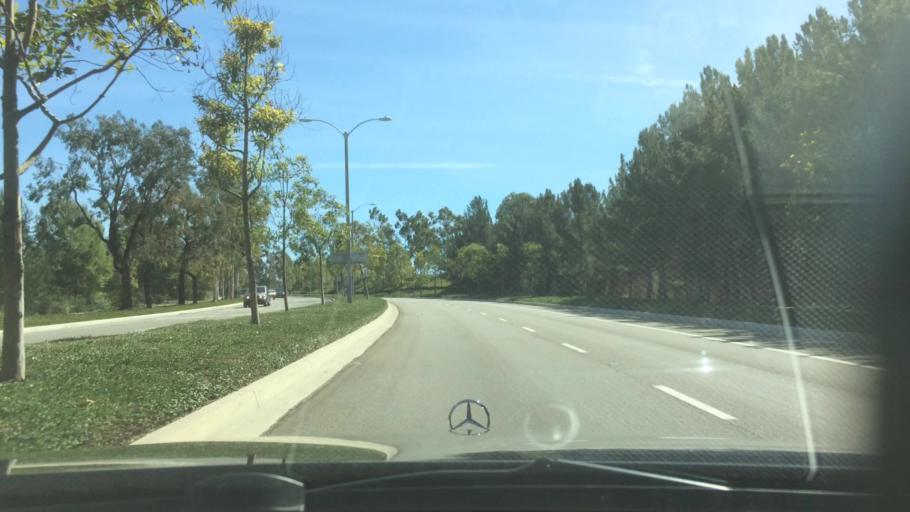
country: US
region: California
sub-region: Orange County
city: San Joaquin Hills
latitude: 33.6302
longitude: -117.8348
